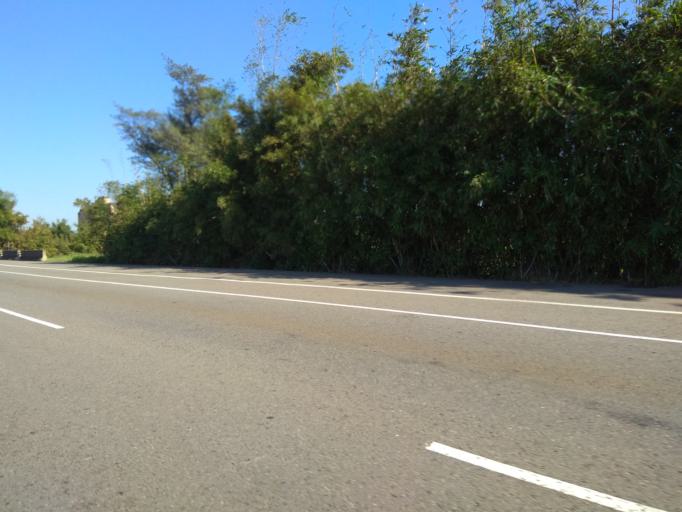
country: TW
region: Taiwan
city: Taoyuan City
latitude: 25.0291
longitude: 121.0920
